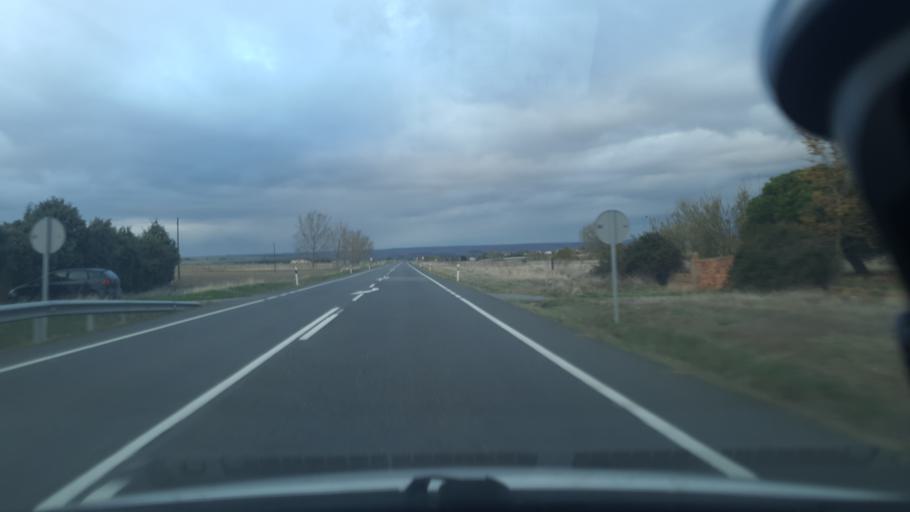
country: ES
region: Castille and Leon
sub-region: Provincia de Segovia
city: Valdeprados
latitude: 40.8642
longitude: -4.2413
